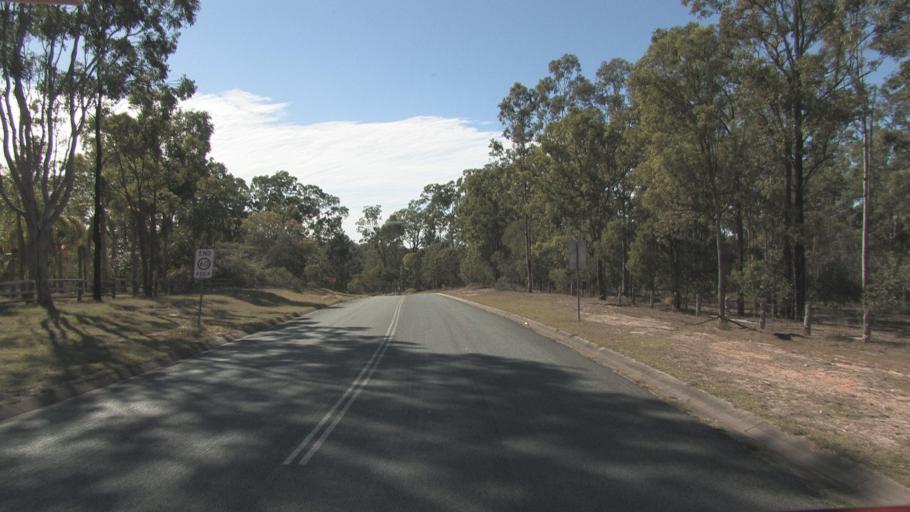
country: AU
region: Queensland
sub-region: Ipswich
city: Springfield Lakes
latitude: -27.7110
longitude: 152.9332
